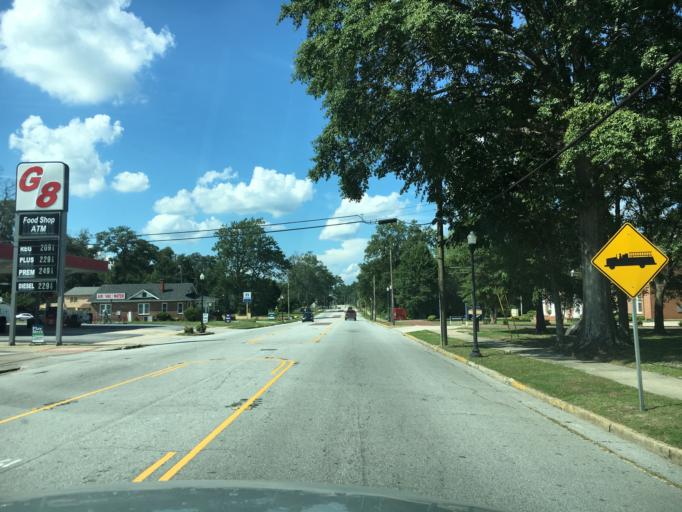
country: US
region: South Carolina
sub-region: Laurens County
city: Clinton
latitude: 34.4763
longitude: -81.8809
